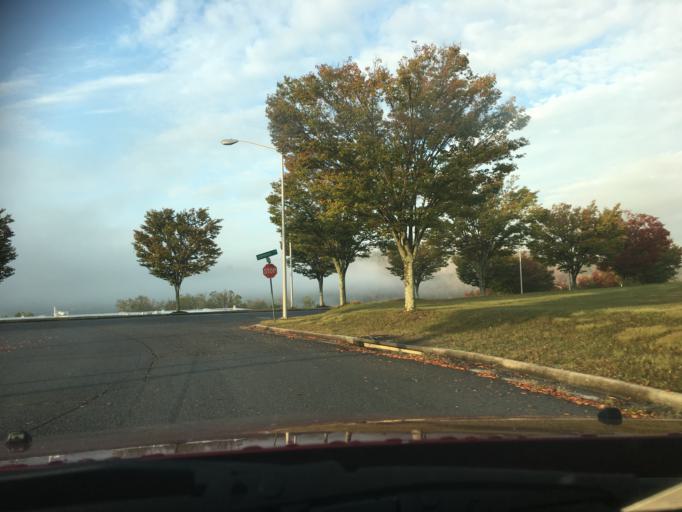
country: US
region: Virginia
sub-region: City of Radford
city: Radford
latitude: 37.0963
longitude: -80.5753
